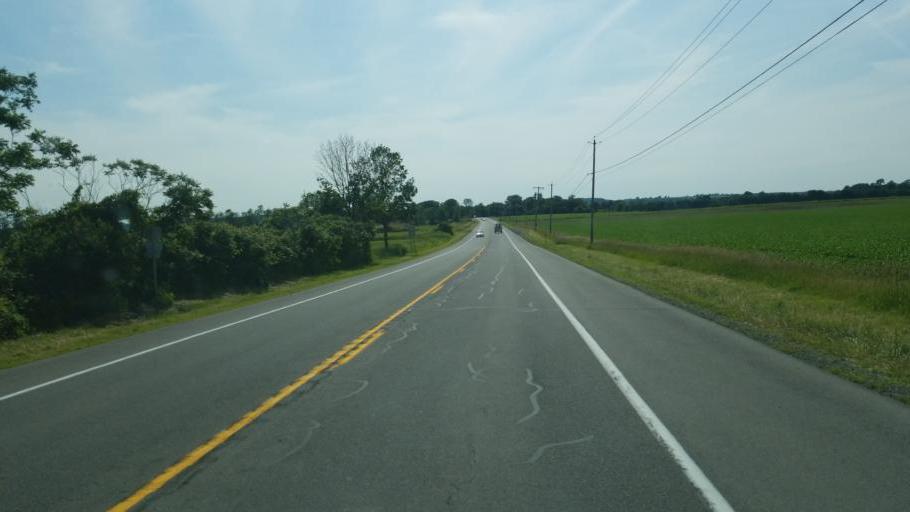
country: US
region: New York
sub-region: Livingston County
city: Lima
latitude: 42.9094
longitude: -77.5741
